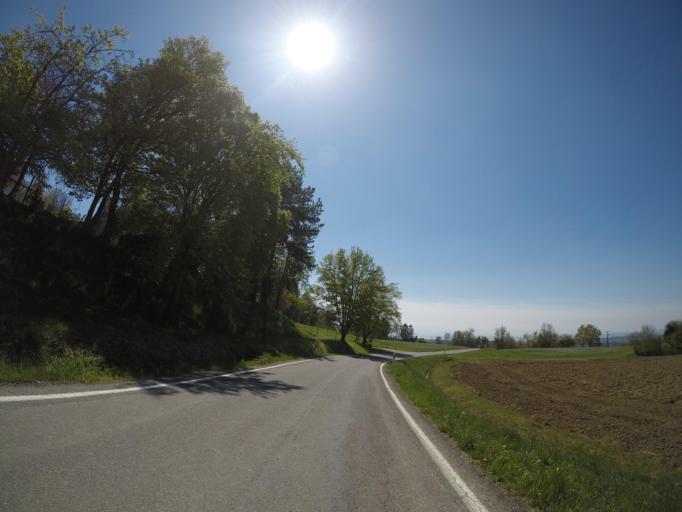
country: DE
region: Baden-Wuerttemberg
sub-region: Tuebingen Region
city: Markdorf
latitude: 47.7393
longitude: 9.3841
